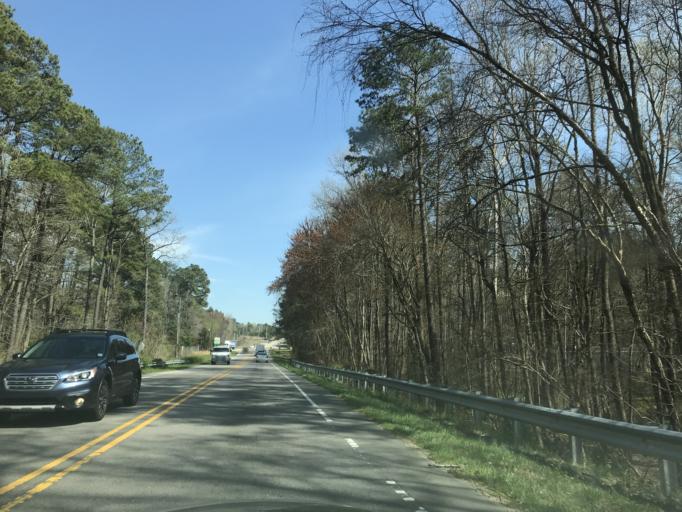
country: US
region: North Carolina
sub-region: Wake County
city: Knightdale
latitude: 35.8480
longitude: -78.5288
